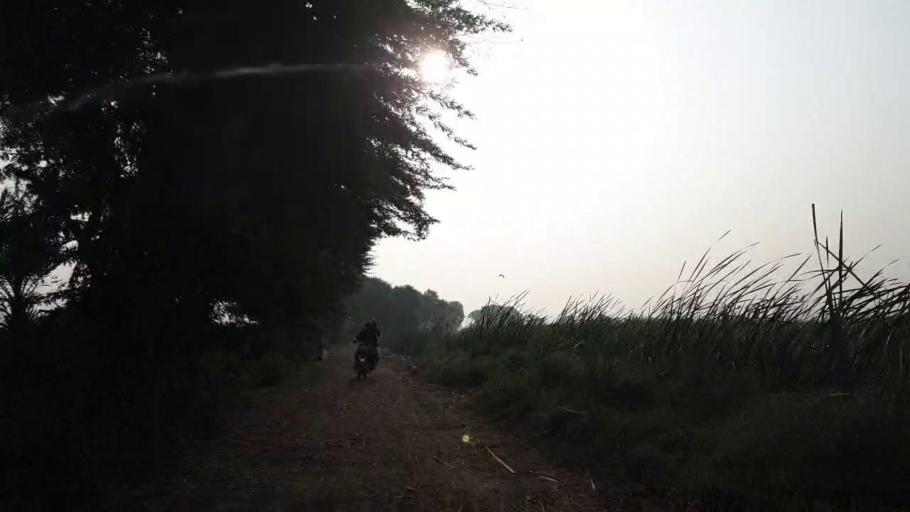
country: PK
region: Sindh
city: Tando Muhammad Khan
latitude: 25.1253
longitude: 68.5600
